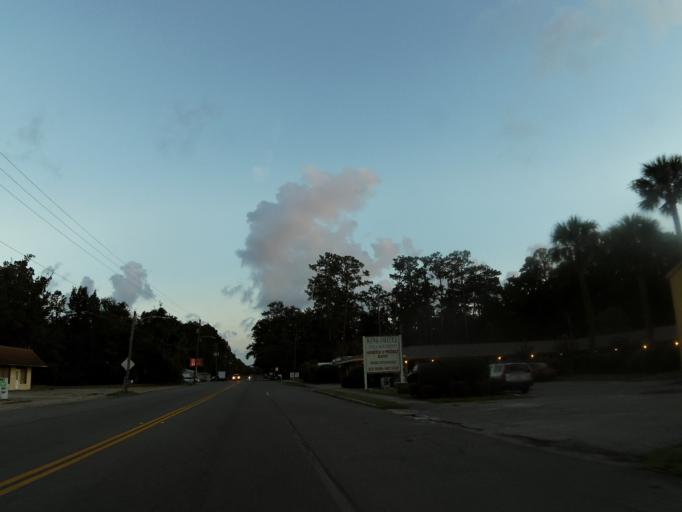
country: US
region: Georgia
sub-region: Camden County
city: Kingsland
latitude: 30.7940
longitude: -81.6891
